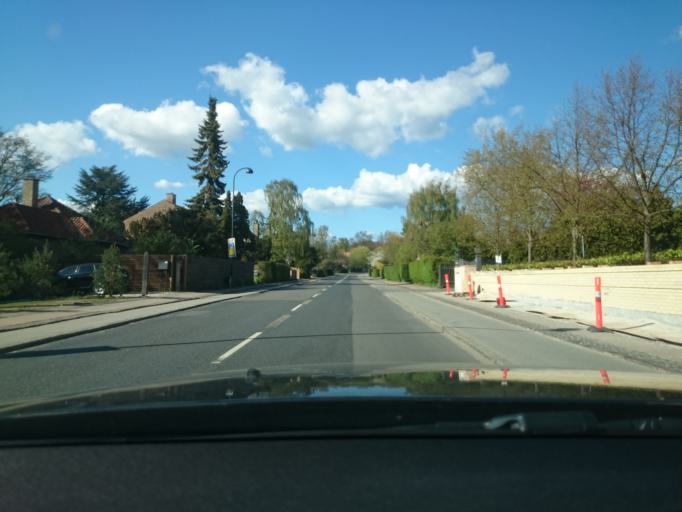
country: DK
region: Capital Region
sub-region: Gentofte Kommune
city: Charlottenlund
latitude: 55.7648
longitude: 12.5587
